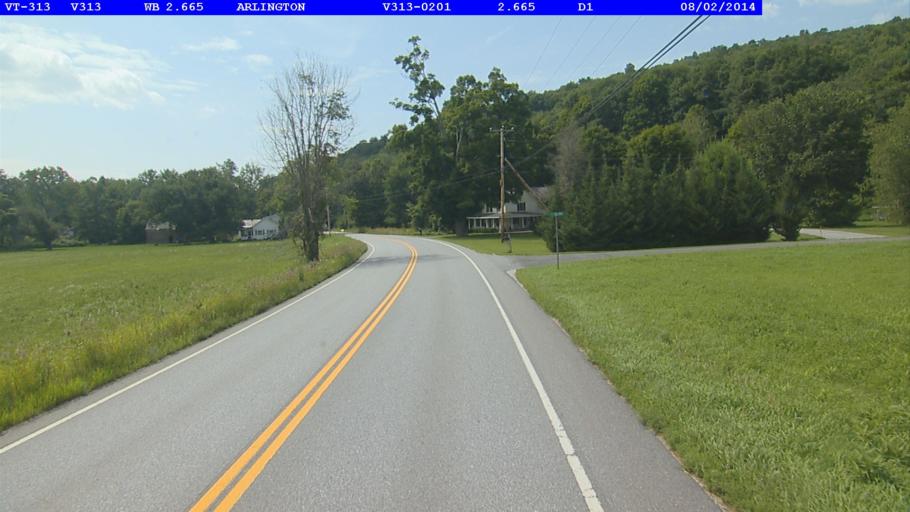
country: US
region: Vermont
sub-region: Bennington County
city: Arlington
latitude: 43.1044
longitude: -73.2155
